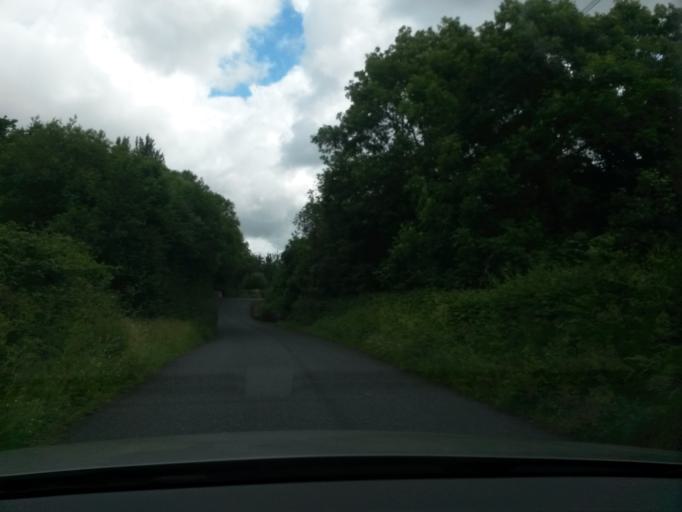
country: IE
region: Connaught
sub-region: Sligo
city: Sligo
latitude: 54.3318
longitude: -8.4325
